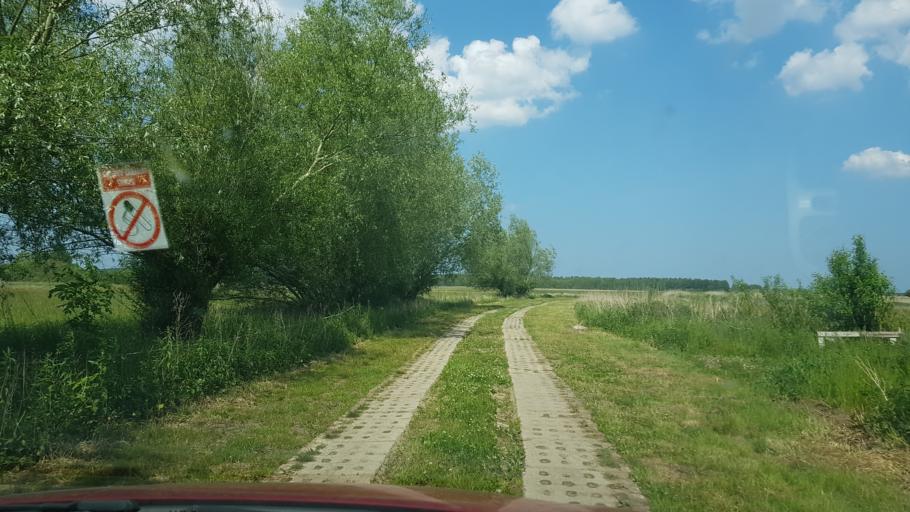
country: PL
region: West Pomeranian Voivodeship
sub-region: Powiat gryficki
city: Trzebiatow
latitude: 54.0940
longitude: 15.2126
